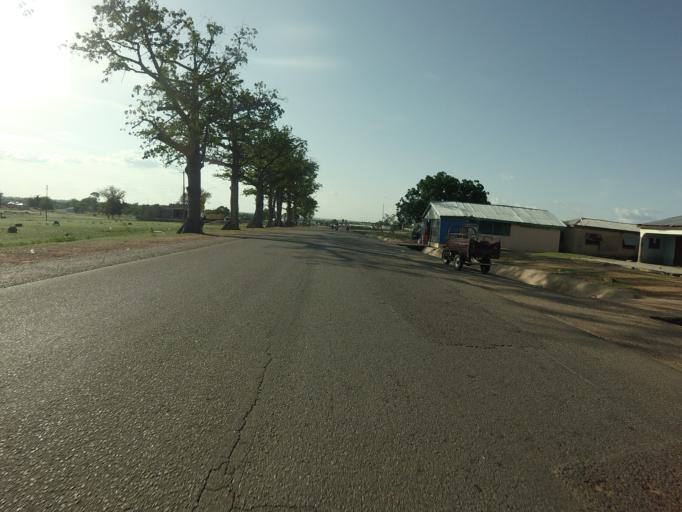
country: GH
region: Upper East
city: Navrongo
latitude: 10.9808
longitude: -1.1062
